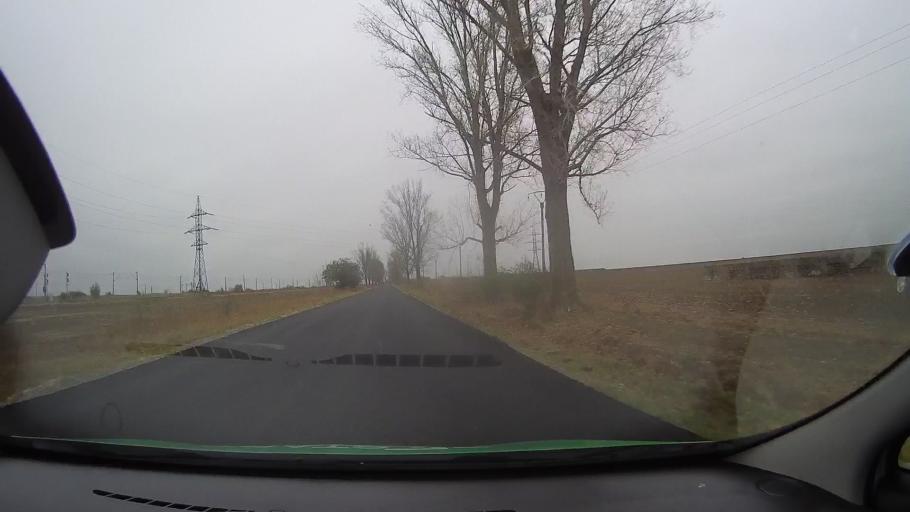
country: RO
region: Ialomita
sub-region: Comuna Valea Ciorii
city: Valea Ciorii
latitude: 44.7518
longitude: 27.5676
